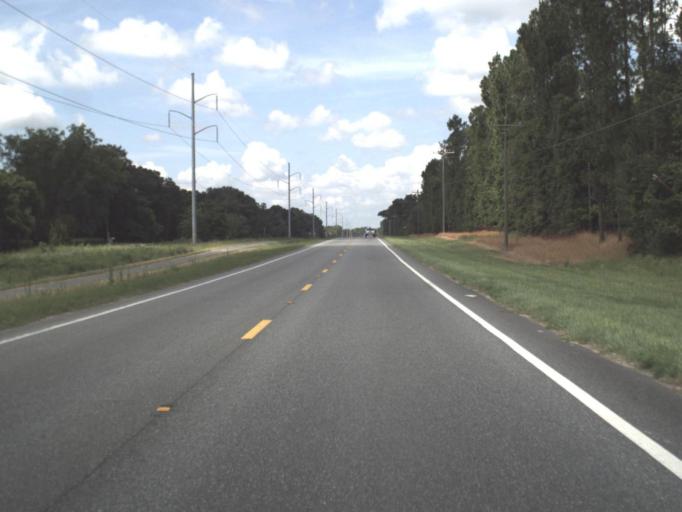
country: US
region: Florida
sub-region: Alachua County
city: Archer
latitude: 29.5574
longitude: -82.4874
